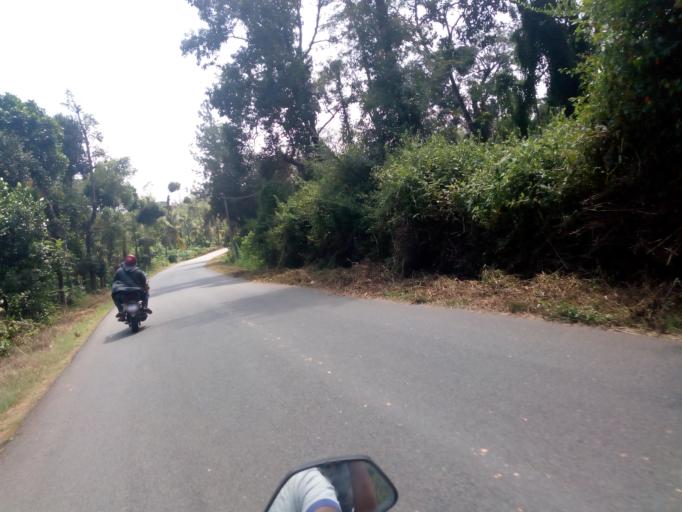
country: IN
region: Karnataka
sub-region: Kodagu
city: Ponnampet
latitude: 12.0650
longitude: 75.9488
